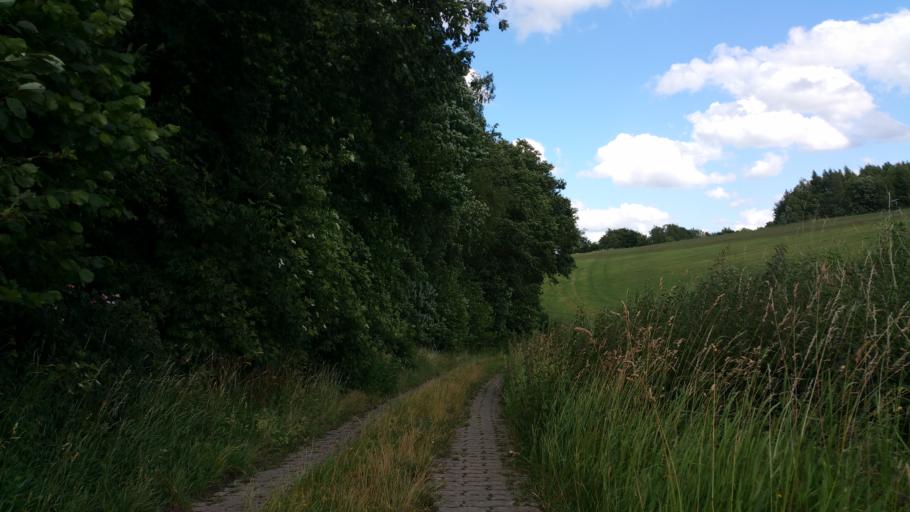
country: DE
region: Bavaria
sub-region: Upper Franconia
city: Schwarzenbach an der Saale
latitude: 50.2309
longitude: 11.9291
